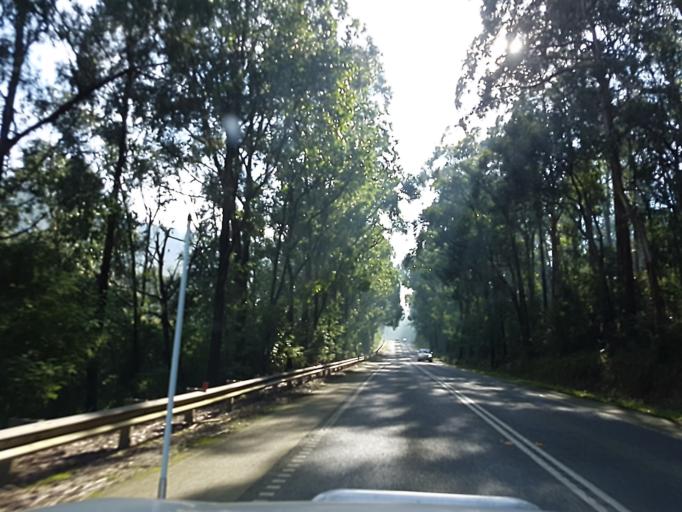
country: AU
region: Victoria
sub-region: Yarra Ranges
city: Yarra Glen
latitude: -37.4937
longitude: 145.4184
